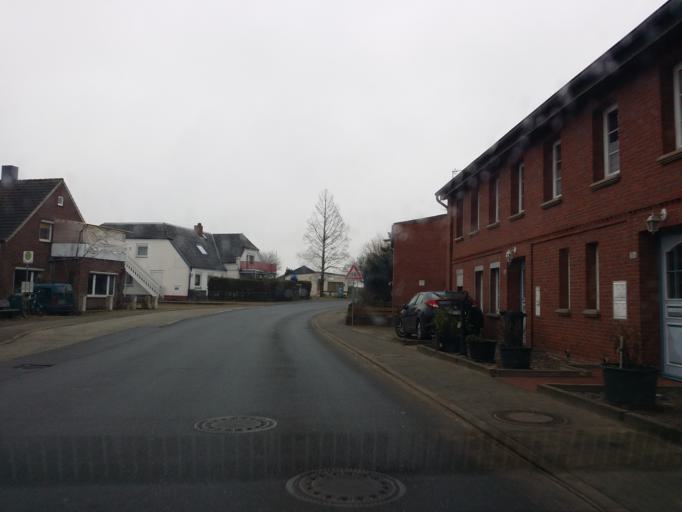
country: DE
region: Schleswig-Holstein
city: Fehmarn
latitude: 54.4513
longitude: 11.1476
